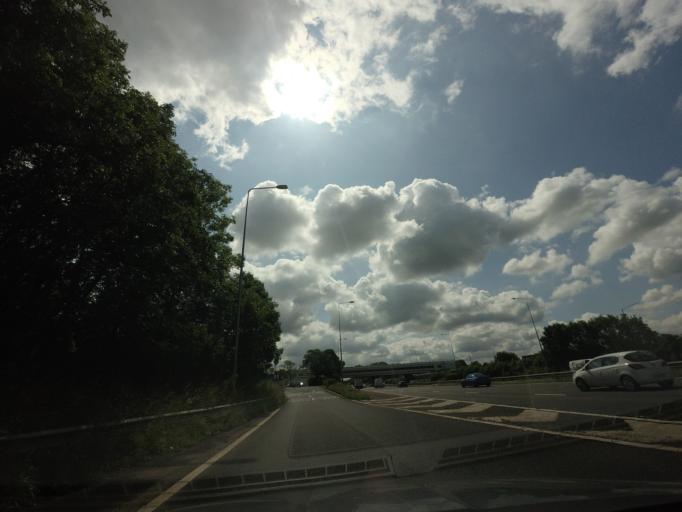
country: GB
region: England
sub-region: Lancashire
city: Coppull
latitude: 53.6329
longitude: -2.6909
